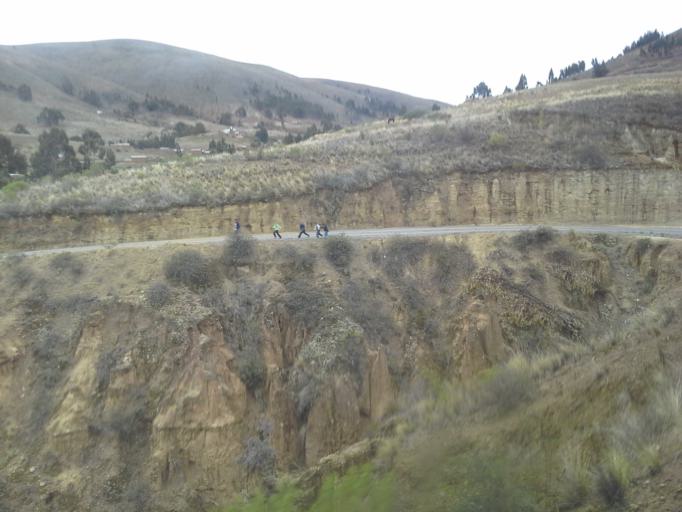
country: BO
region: Cochabamba
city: Colomi
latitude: -17.4147
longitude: -65.8045
